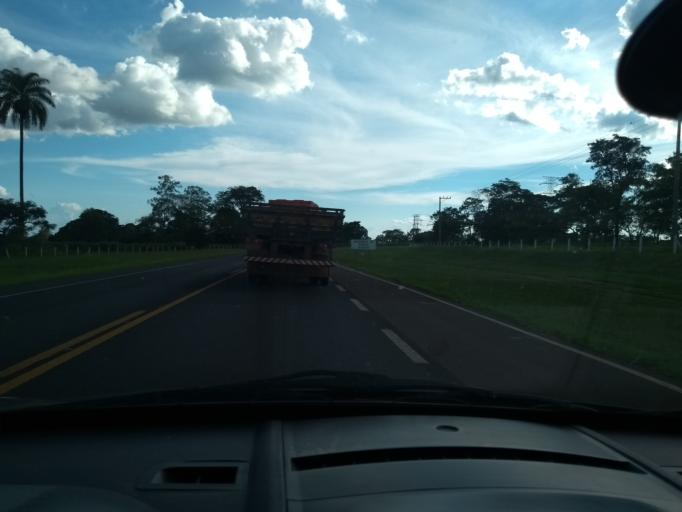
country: BR
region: Sao Paulo
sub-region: Casa Branca
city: Casa Branca
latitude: -21.7962
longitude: -47.0747
